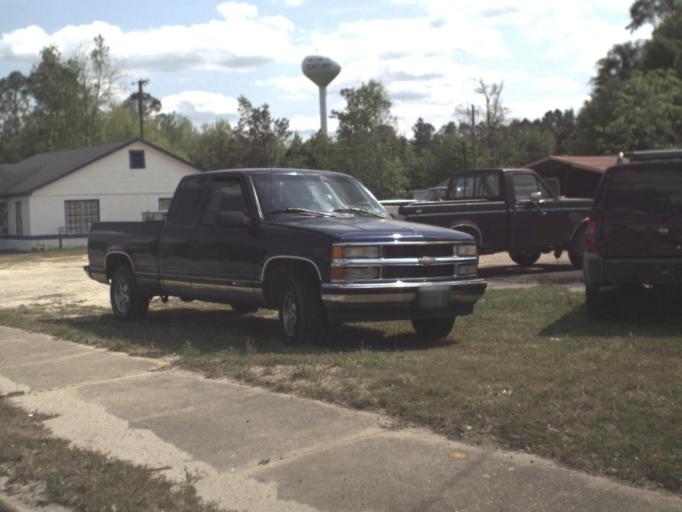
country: US
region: Alabama
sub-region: Escambia County
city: Flomaton
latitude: 30.9957
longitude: -87.2592
